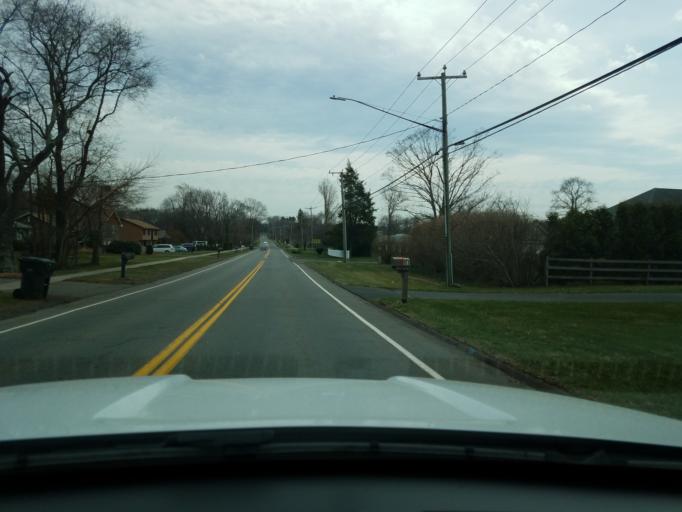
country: US
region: Connecticut
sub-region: Hartford County
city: Newington
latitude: 41.6669
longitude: -72.6875
